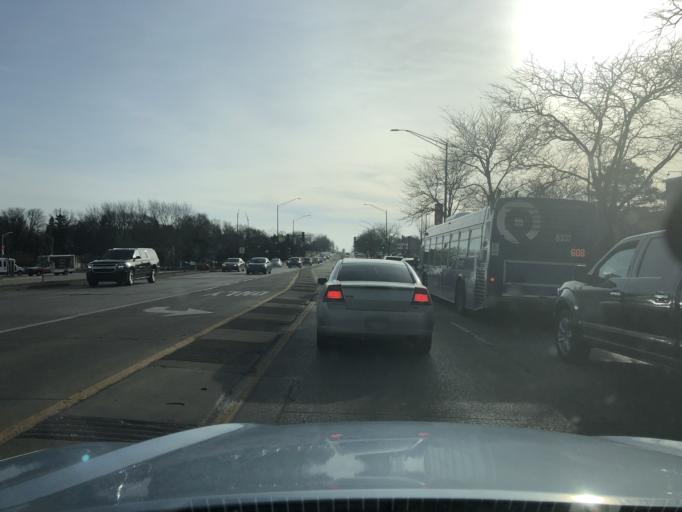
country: US
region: Illinois
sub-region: DuPage County
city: Roselle
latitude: 42.0067
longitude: -88.0801
